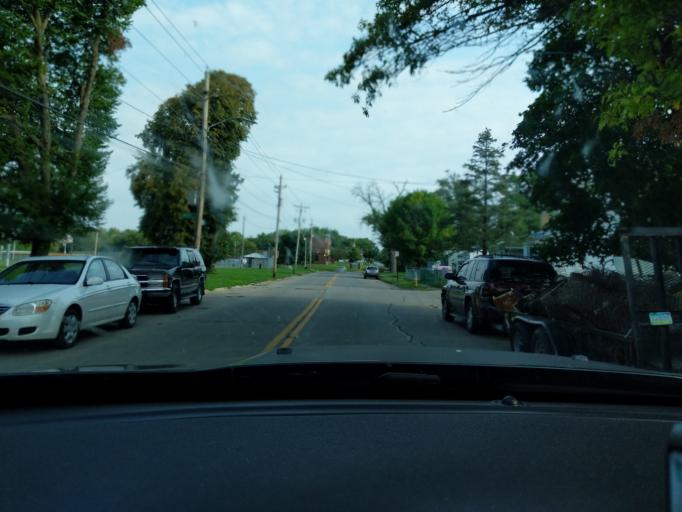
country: US
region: Illinois
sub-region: Rock Island County
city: Rock Island
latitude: 41.5045
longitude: -90.6244
